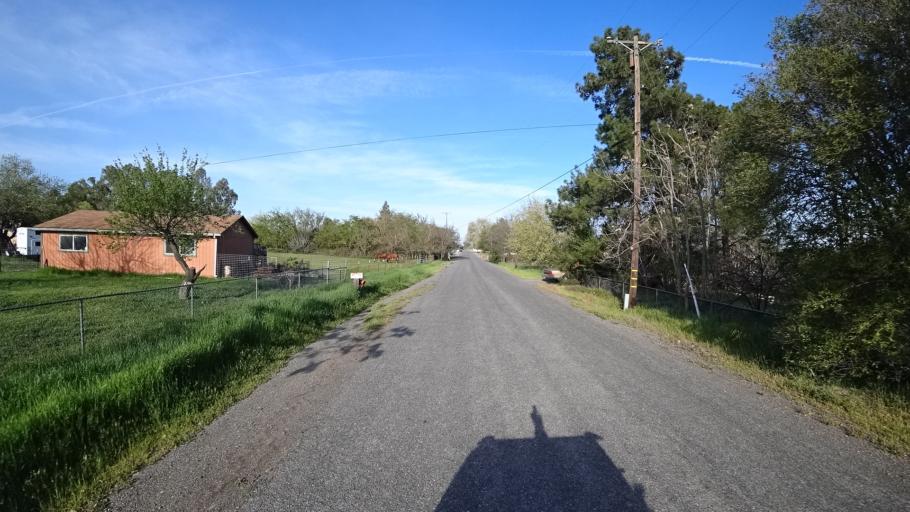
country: US
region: California
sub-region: Glenn County
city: Orland
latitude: 39.7150
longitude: -122.2163
